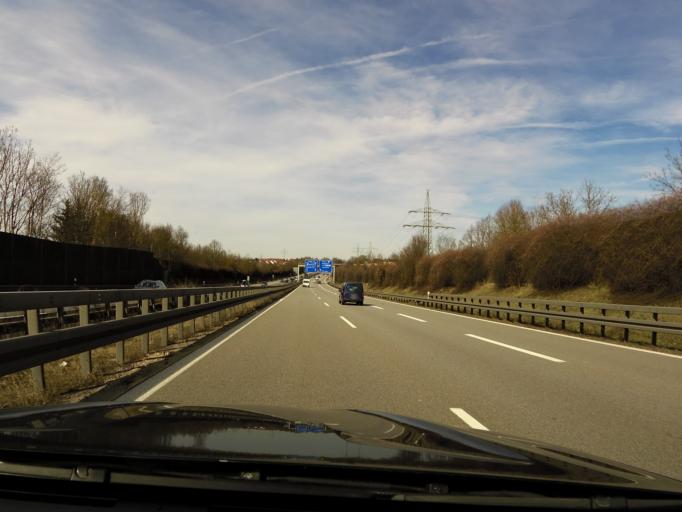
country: DE
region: Bavaria
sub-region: Upper Palatinate
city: Pentling
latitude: 48.9809
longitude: 12.0629
